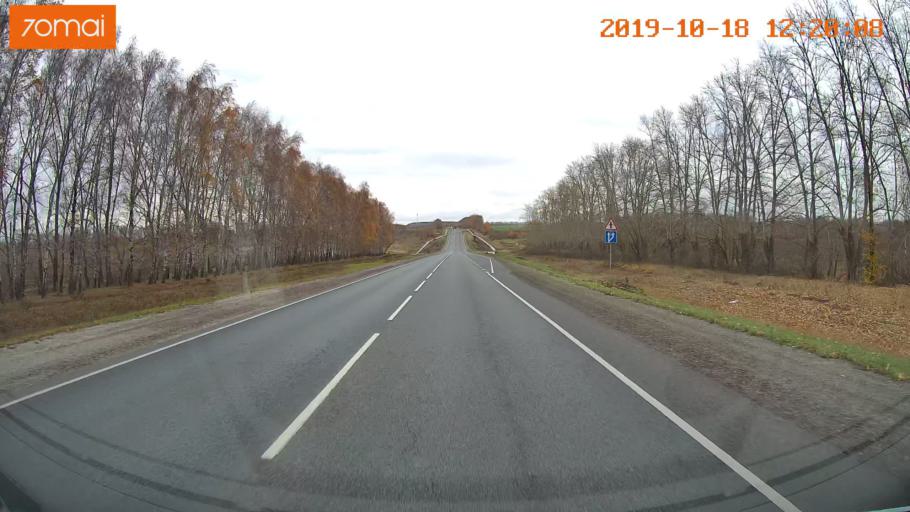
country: RU
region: Rjazan
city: Bagramovo
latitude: 54.4928
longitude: 39.4765
